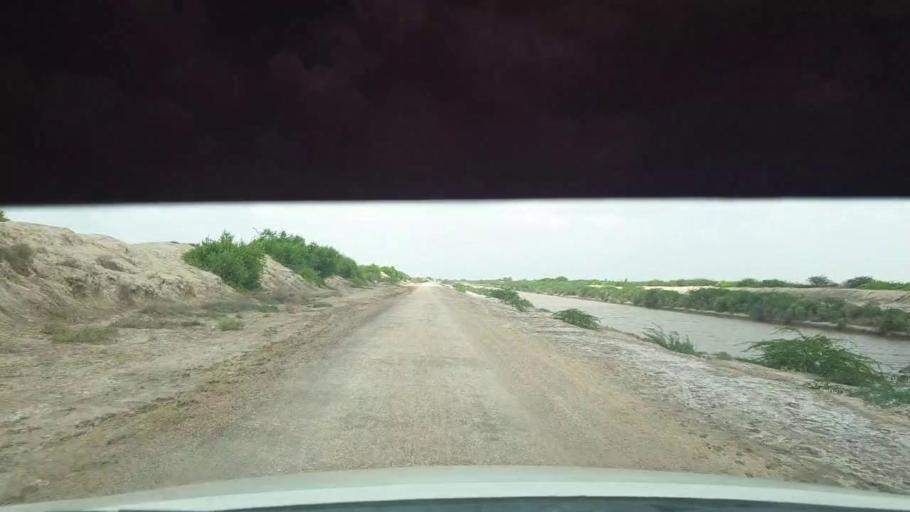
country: PK
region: Sindh
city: Kadhan
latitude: 24.5097
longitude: 69.1189
